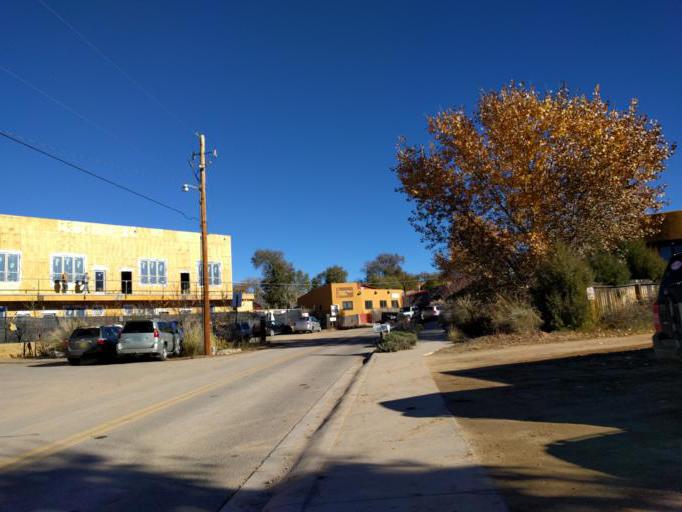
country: US
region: New Mexico
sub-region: Santa Fe County
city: Santa Fe
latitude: 35.6649
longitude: -105.9647
